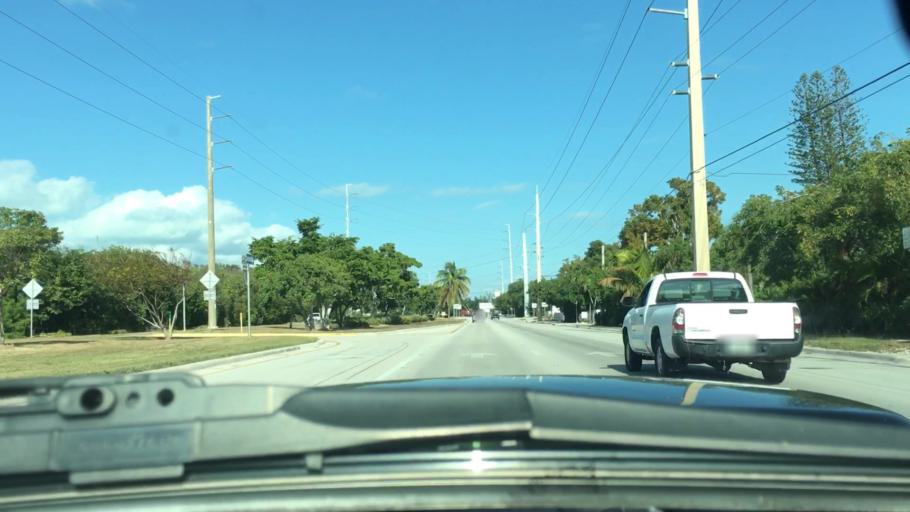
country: US
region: Florida
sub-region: Monroe County
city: Tavernier
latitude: 25.0113
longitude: -80.5150
